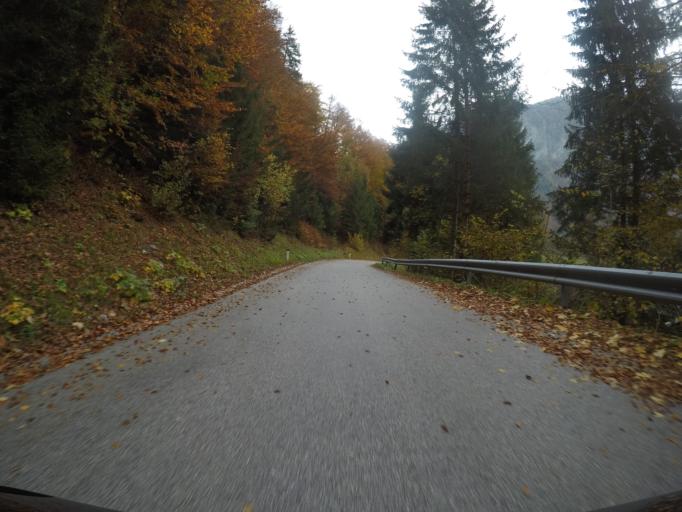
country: SI
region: Kranjska Gora
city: Mojstrana
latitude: 46.4323
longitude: 13.9341
